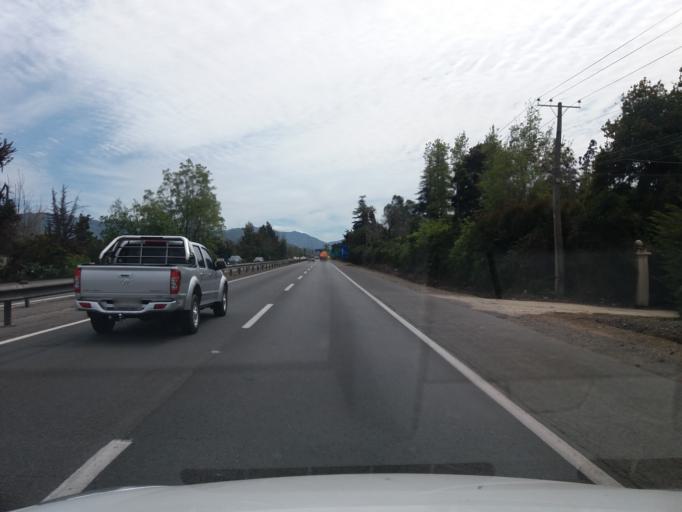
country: CL
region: Valparaiso
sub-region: Provincia de Quillota
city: Hacienda La Calera
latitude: -32.7288
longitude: -71.2018
